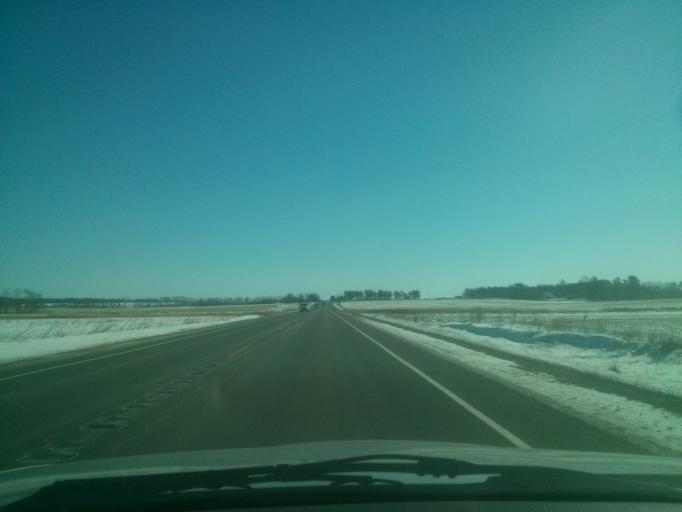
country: US
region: Wisconsin
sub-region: Polk County
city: Clear Lake
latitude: 45.1364
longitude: -92.3604
